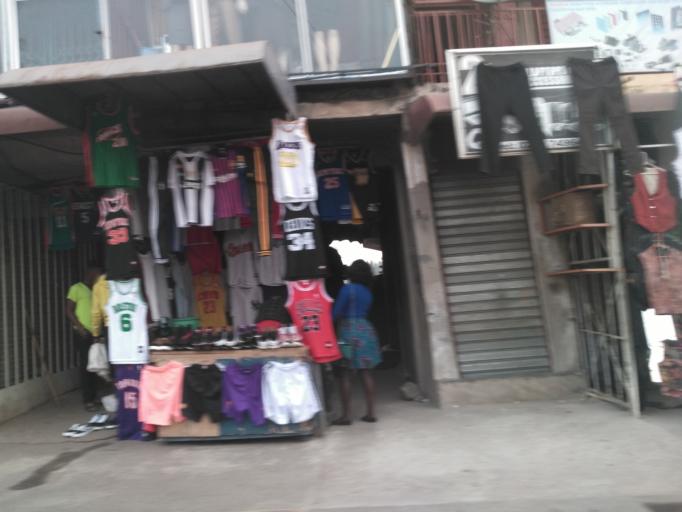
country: GH
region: Ashanti
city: Kumasi
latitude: 6.6921
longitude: -1.6203
